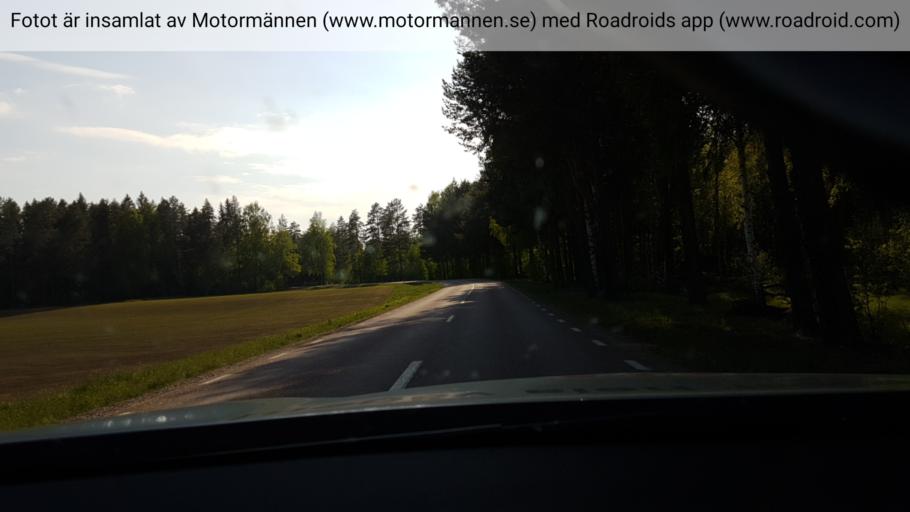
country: SE
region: Gaevleborg
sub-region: Sandvikens Kommun
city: Arsunda
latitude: 60.4508
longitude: 16.6974
